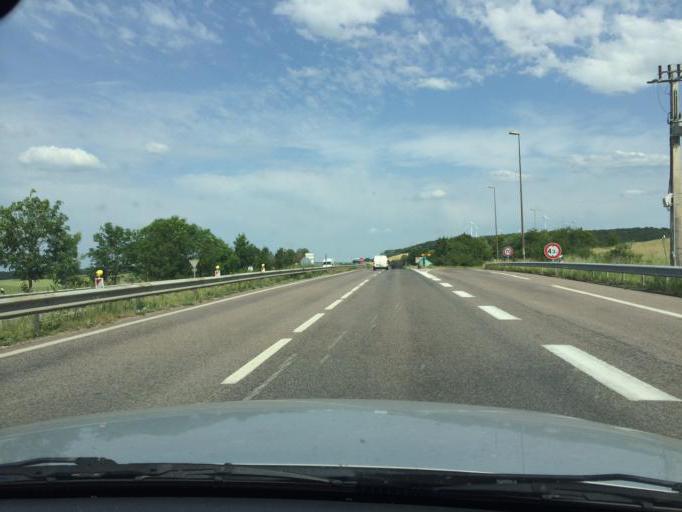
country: FR
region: Lorraine
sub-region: Departement de la Meuse
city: Lerouville
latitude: 48.7053
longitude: 5.4613
